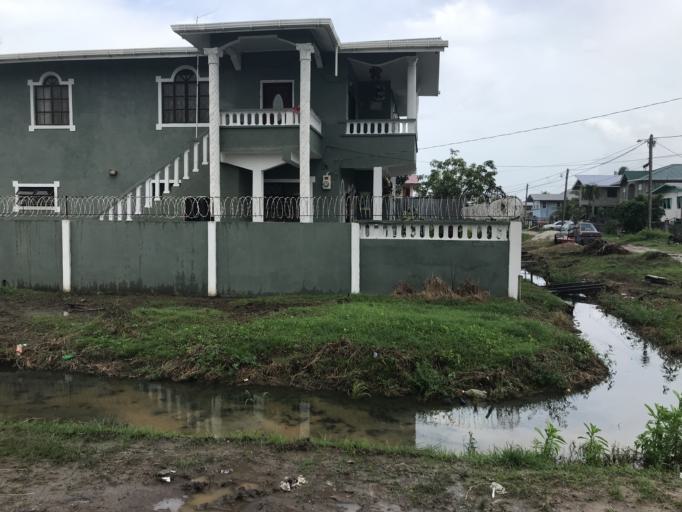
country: GY
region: Demerara-Mahaica
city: Georgetown
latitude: 6.8053
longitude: -58.1193
